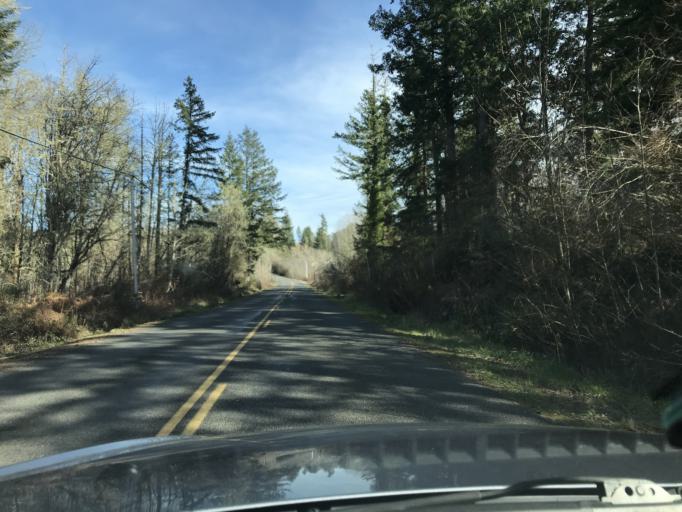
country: US
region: Washington
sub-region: Pierce County
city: Home
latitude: 47.2503
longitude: -122.7550
